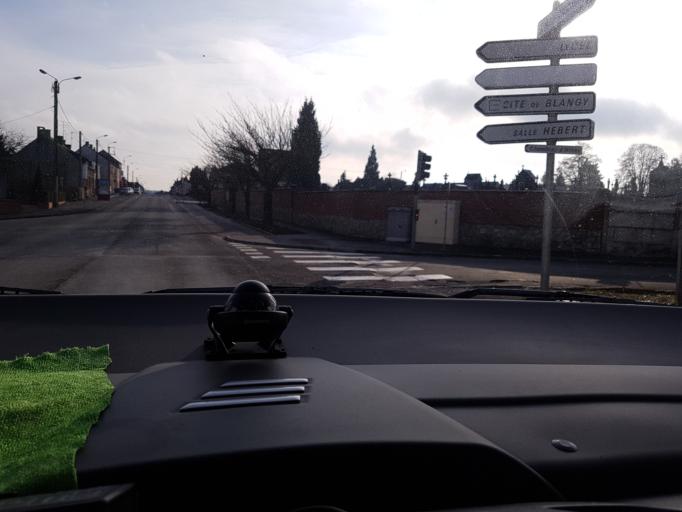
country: FR
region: Picardie
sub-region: Departement de l'Aisne
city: Hirson
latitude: 49.9309
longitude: 4.0741
